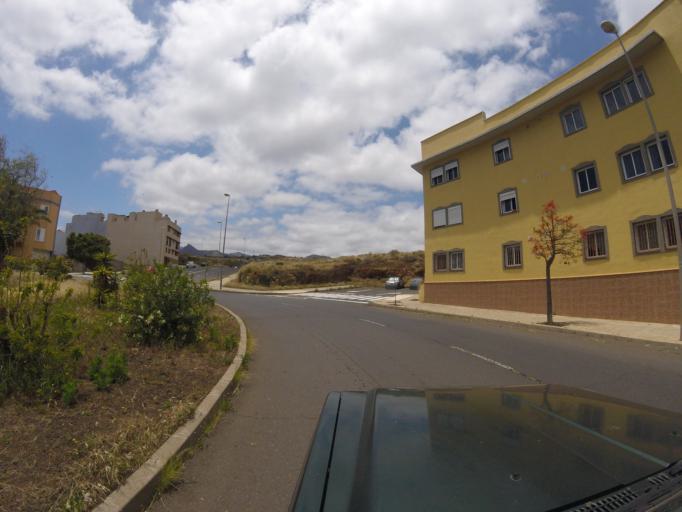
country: ES
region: Canary Islands
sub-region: Provincia de Santa Cruz de Tenerife
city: La Laguna
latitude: 28.4476
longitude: -16.3131
